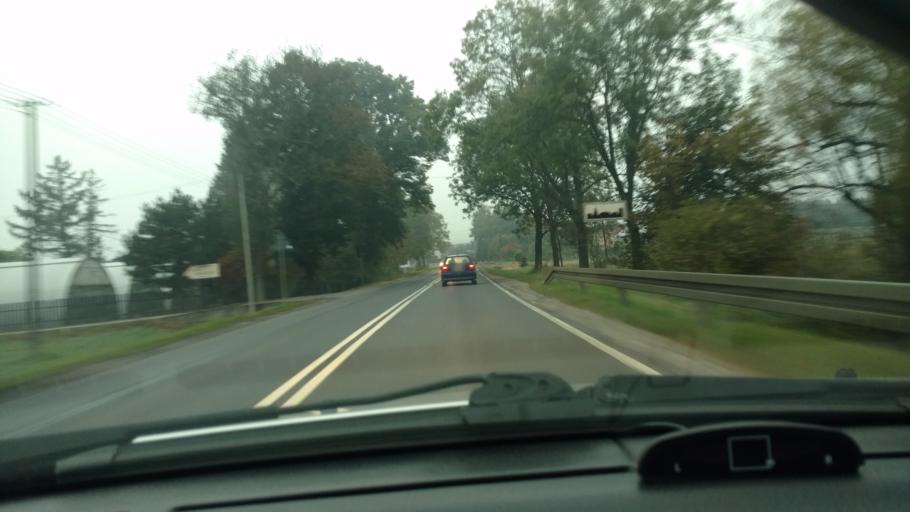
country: PL
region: Subcarpathian Voivodeship
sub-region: Powiat strzyzowski
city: Strzyzow
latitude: 49.8749
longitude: 21.7607
